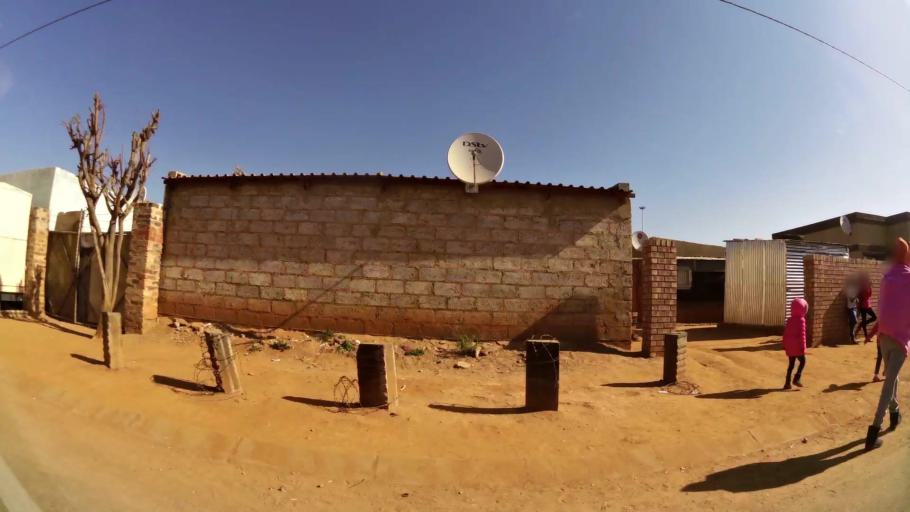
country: ZA
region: Gauteng
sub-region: Ekurhuleni Metropolitan Municipality
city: Tembisa
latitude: -26.0255
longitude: 28.2381
